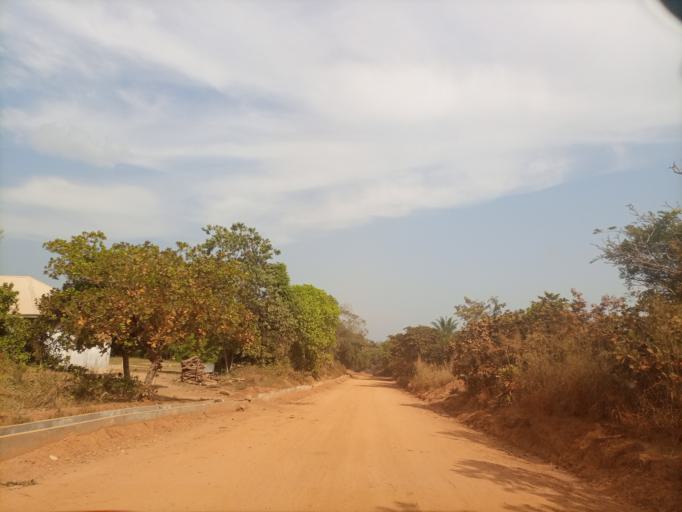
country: NG
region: Enugu
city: Opi
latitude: 6.8103
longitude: 7.5211
